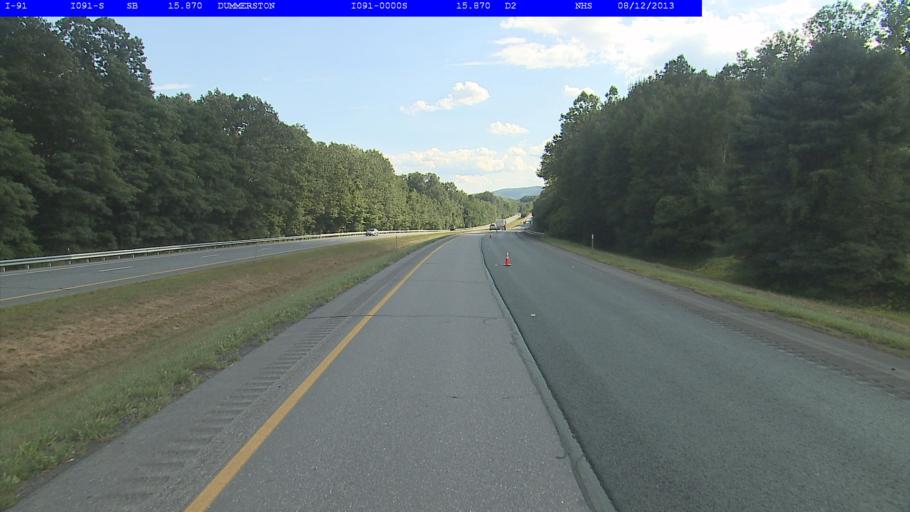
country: US
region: New Hampshire
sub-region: Cheshire County
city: Chesterfield
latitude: 42.9388
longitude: -72.5275
